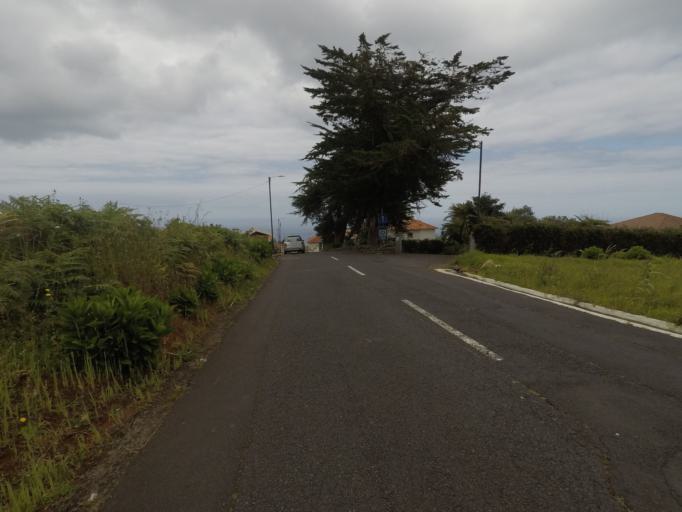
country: PT
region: Madeira
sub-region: Santana
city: Santana
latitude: 32.8055
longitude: -16.8763
